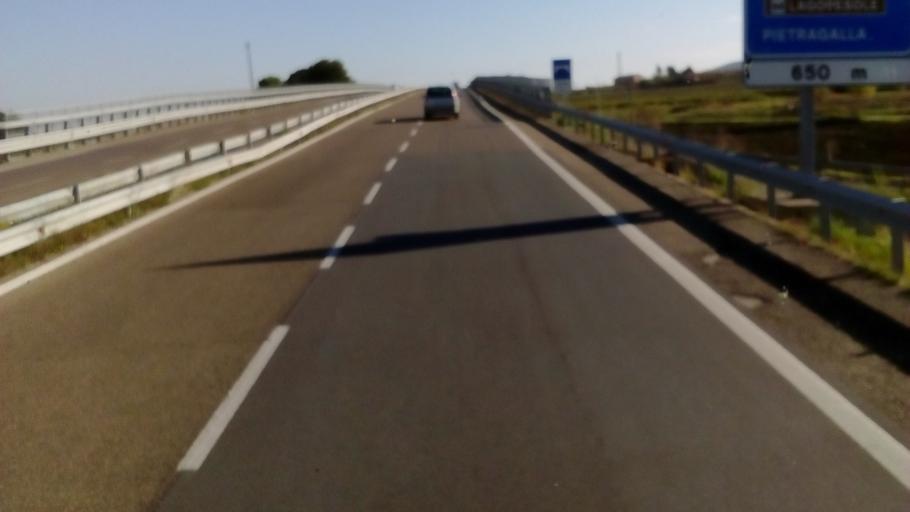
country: IT
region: Basilicate
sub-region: Provincia di Potenza
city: Zona 179
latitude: 41.0865
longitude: 15.6000
